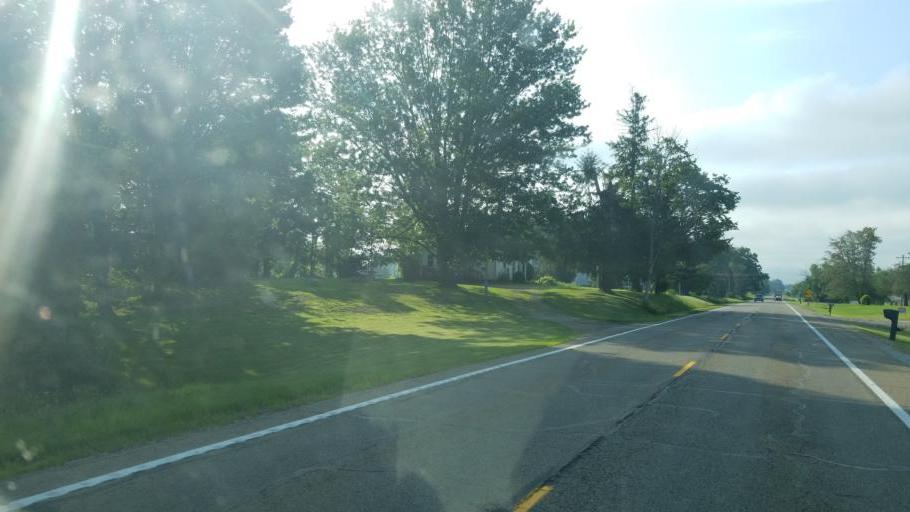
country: US
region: Ohio
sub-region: Morrow County
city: Mount Gilead
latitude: 40.5168
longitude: -82.7459
